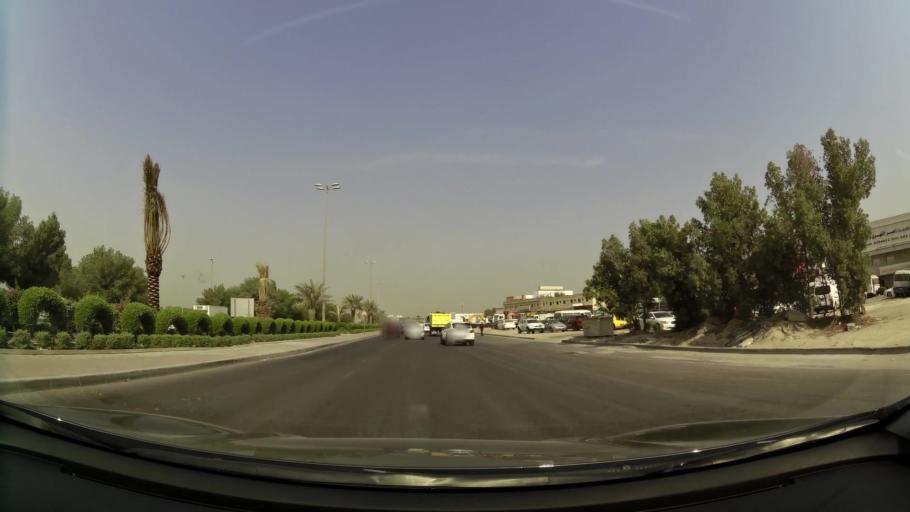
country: KW
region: Al Asimah
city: Ar Rabiyah
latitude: 29.3160
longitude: 47.9260
